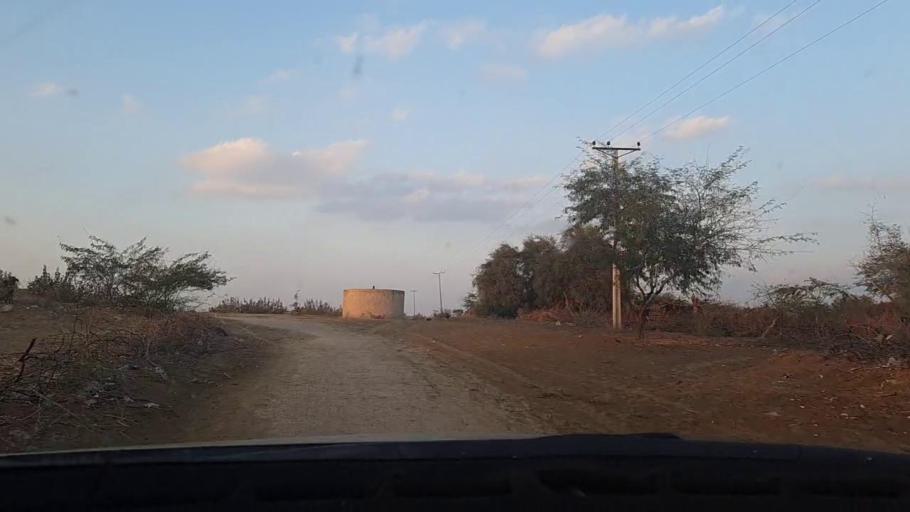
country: PK
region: Sindh
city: Tando Mittha Khan
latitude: 25.9496
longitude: 69.3442
